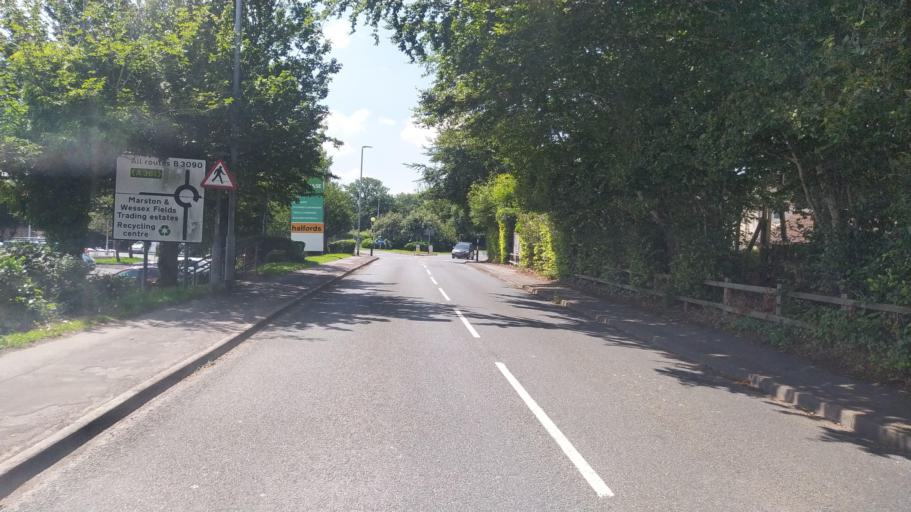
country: GB
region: England
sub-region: Somerset
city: Frome
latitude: 51.2179
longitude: -2.3334
